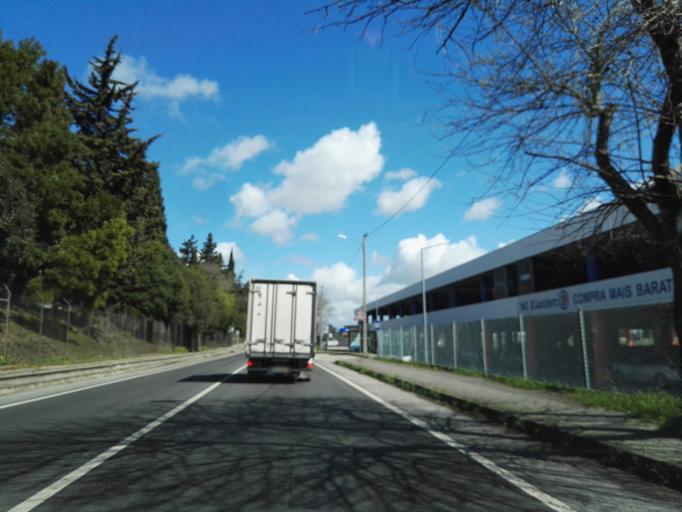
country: PT
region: Lisbon
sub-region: Loures
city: Bobadela
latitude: 38.8098
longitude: -9.0943
